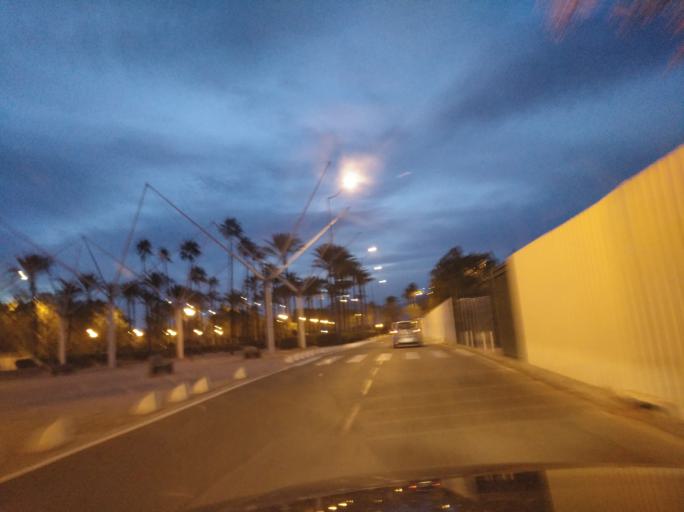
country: ES
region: Andalusia
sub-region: Provincia de Sevilla
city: Camas
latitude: 37.4066
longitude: -6.0076
